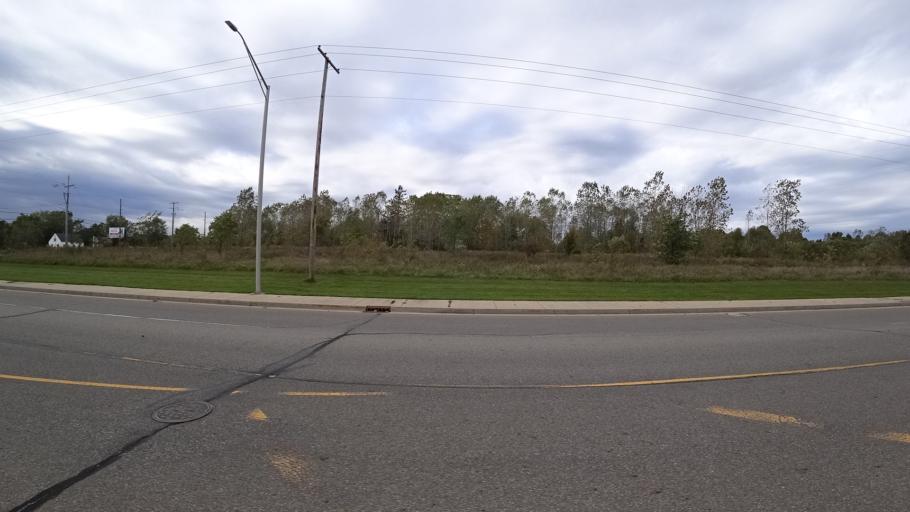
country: US
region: Indiana
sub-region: LaPorte County
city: Trail Creek
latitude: 41.6665
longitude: -86.8846
